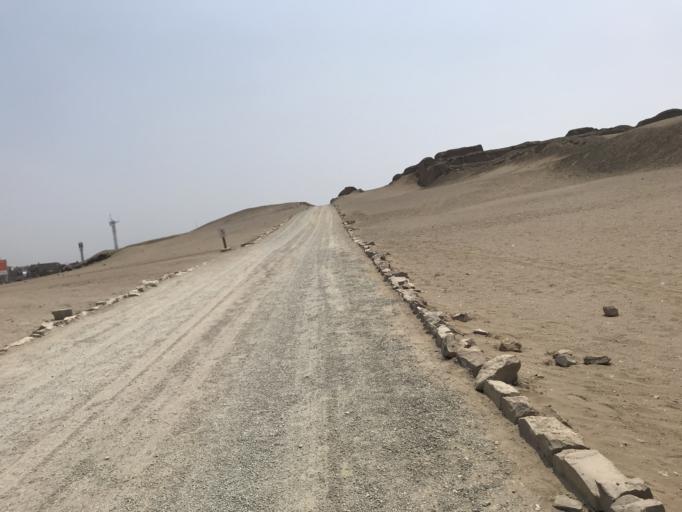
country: PE
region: Lima
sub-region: Lima
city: Punta Hermosa
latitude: -12.2551
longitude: -76.8999
